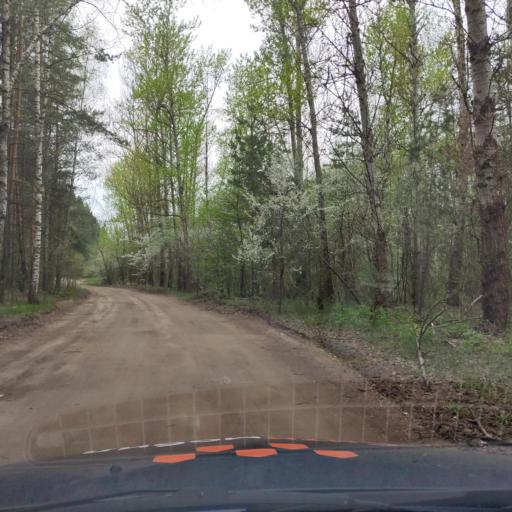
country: RU
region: Voronezj
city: Podgornoye
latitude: 51.8680
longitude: 39.1638
